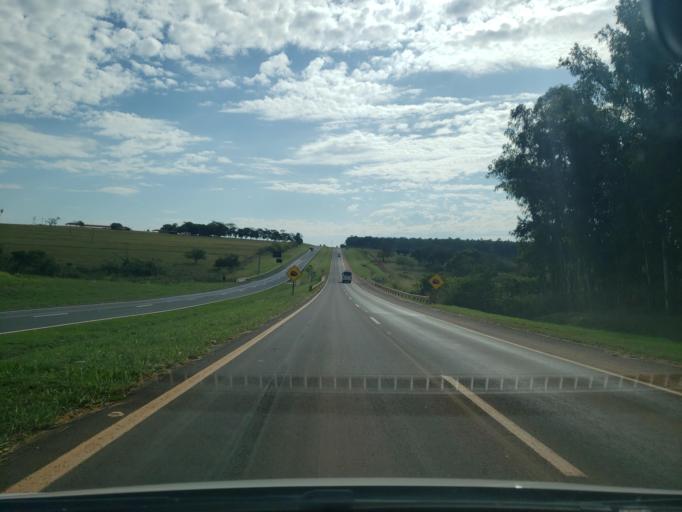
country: BR
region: Sao Paulo
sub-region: Promissao
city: Promissao
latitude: -21.6105
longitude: -49.8695
